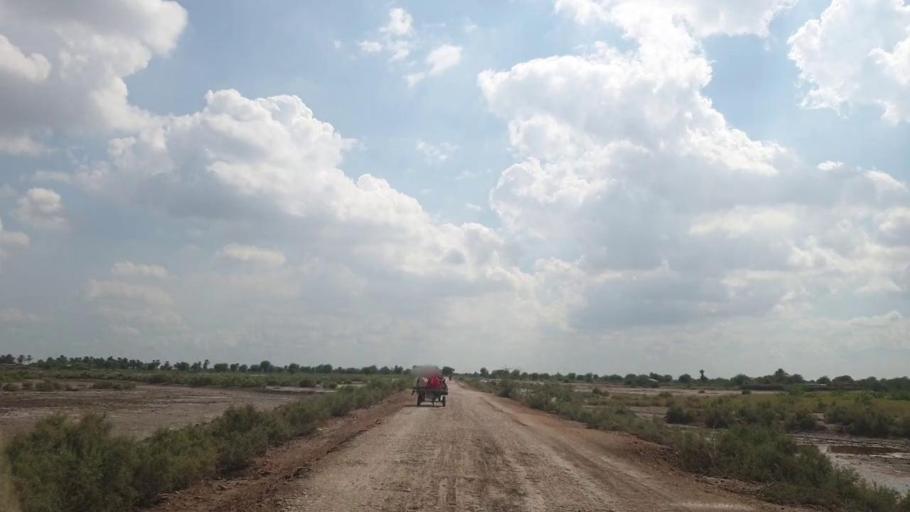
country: PK
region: Sindh
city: Pithoro
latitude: 25.5805
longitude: 69.3855
